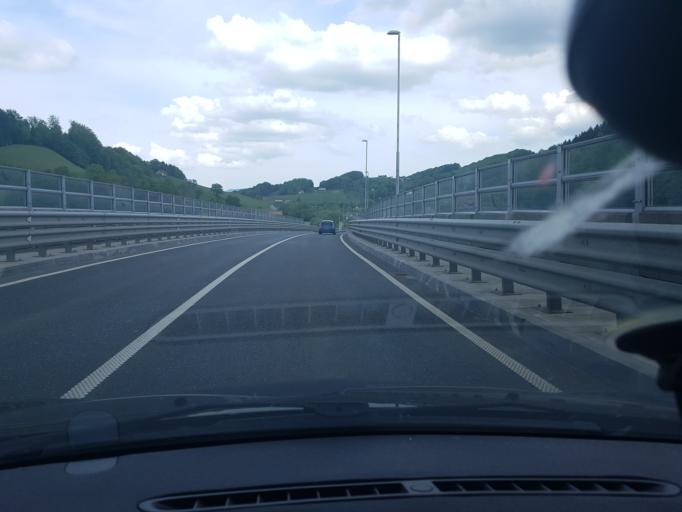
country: SI
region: Sentjur pri Celju
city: Sentjur
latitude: 46.2150
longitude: 15.4417
